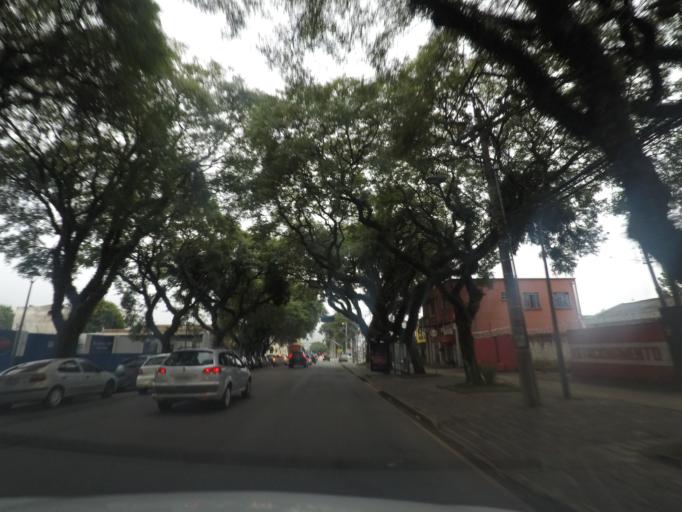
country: BR
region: Parana
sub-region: Curitiba
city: Curitiba
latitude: -25.4433
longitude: -49.2674
